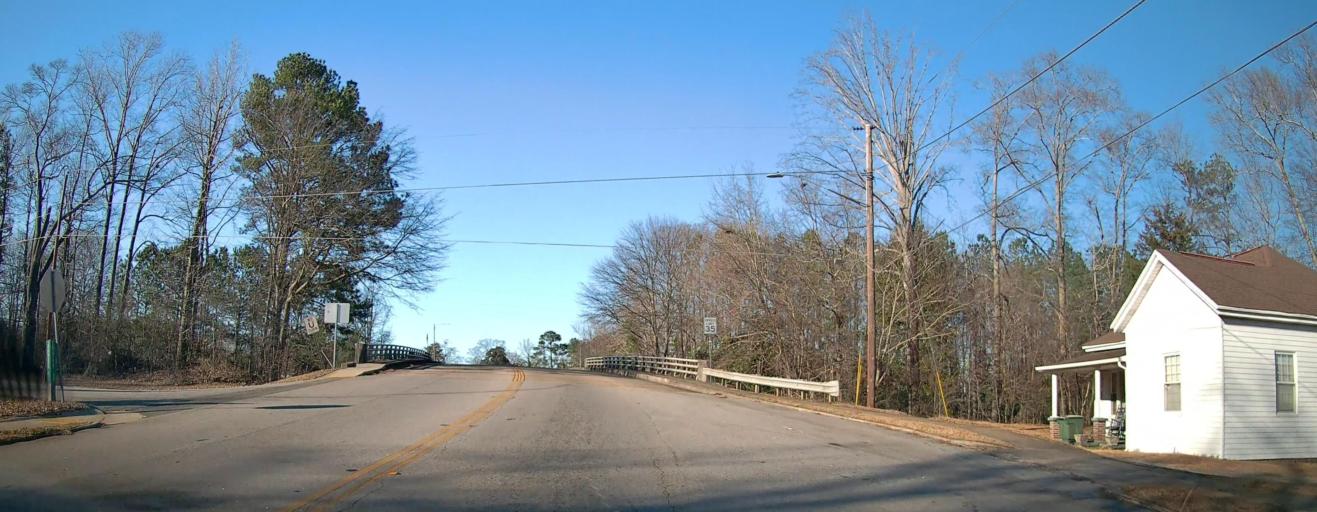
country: US
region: Georgia
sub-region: Meriwether County
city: Manchester
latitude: 32.8572
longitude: -84.6104
